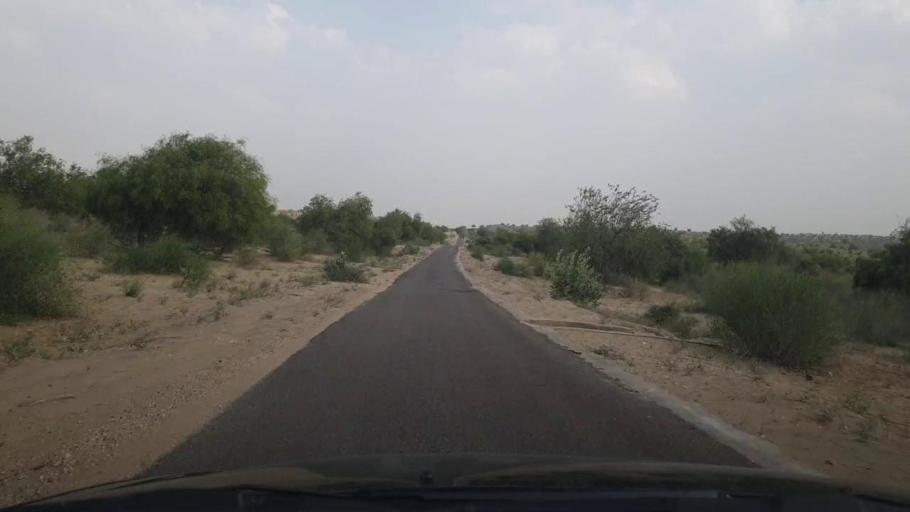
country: PK
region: Sindh
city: Islamkot
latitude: 25.0078
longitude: 70.6530
